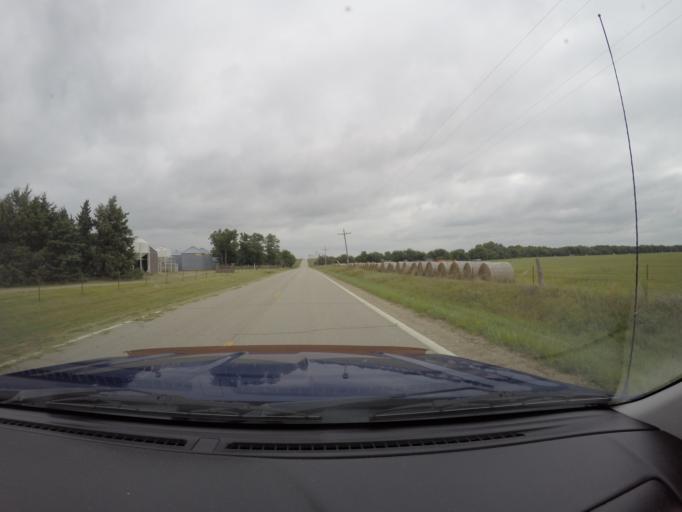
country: US
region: Kansas
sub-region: Morris County
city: Council Grove
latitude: 38.8325
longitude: -96.5941
